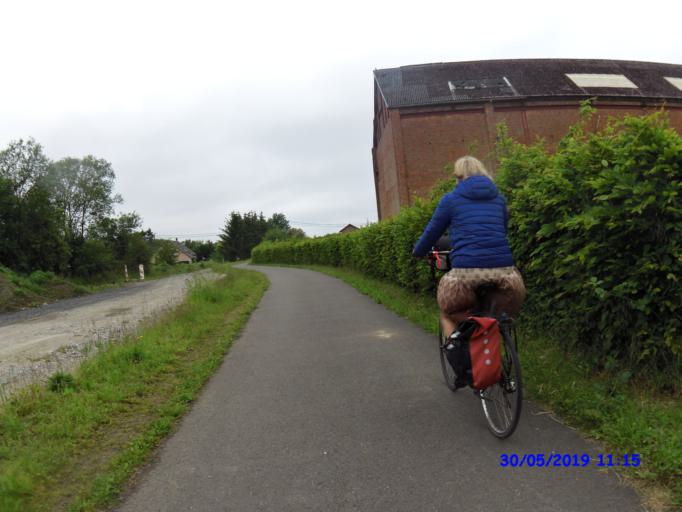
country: BE
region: Wallonia
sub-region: Province du Hainaut
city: Thuin
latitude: 50.3036
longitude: 4.3299
